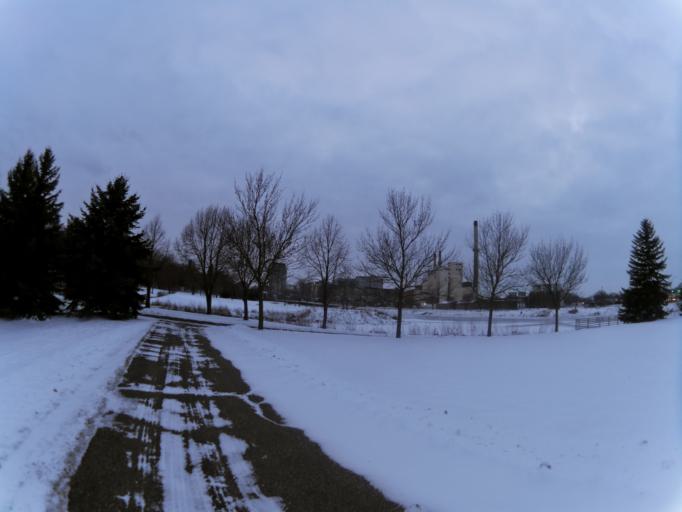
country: US
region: Minnesota
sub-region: Olmsted County
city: Rochester
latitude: 44.0300
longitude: -92.4566
